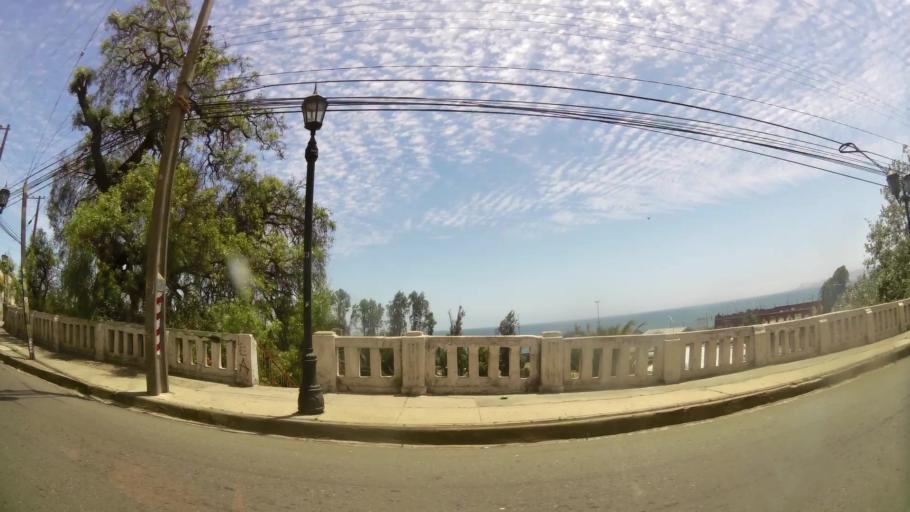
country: CL
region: Valparaiso
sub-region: Provincia de Valparaiso
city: Valparaiso
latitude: -33.0385
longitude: -71.6002
